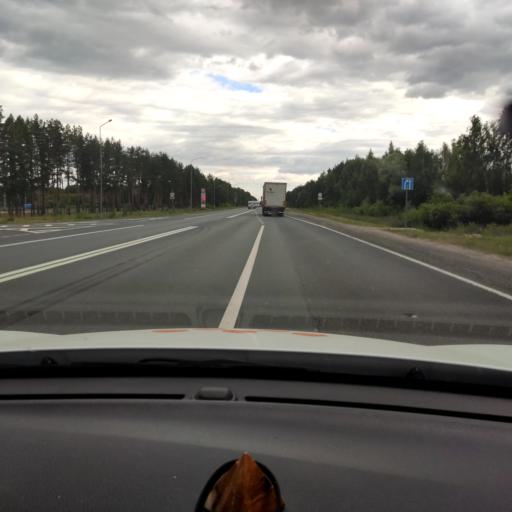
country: RU
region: Mariy-El
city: Pomary
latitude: 55.9449
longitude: 48.3694
